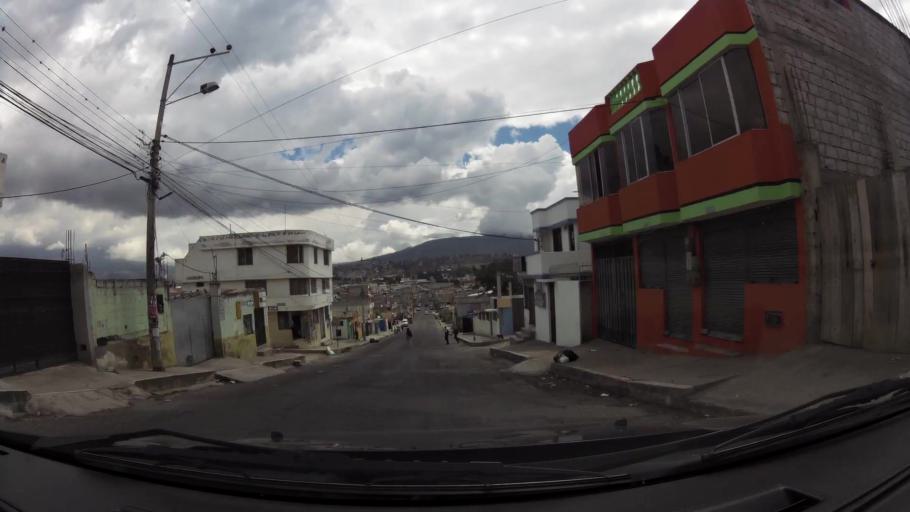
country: EC
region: Pichincha
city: Quito
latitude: -0.0812
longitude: -78.4108
